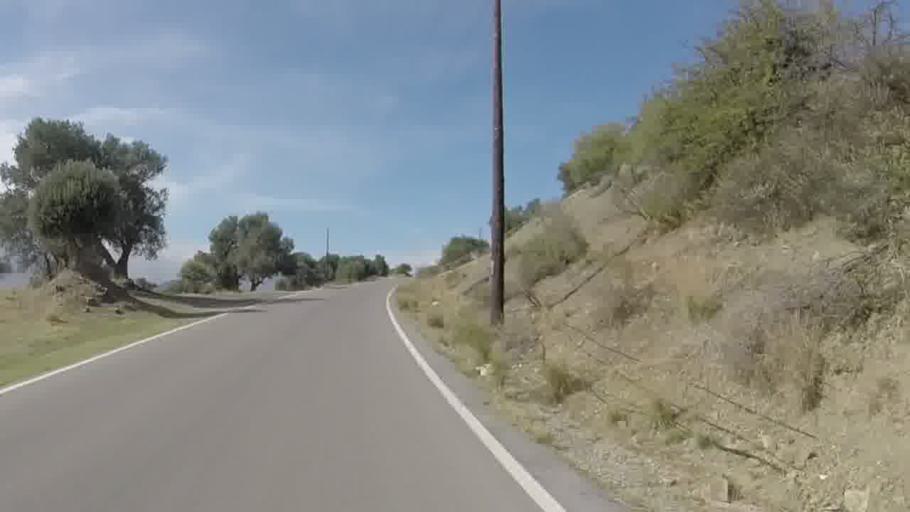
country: GR
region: Crete
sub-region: Nomos Rethymnis
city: Agia Galini
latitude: 35.1471
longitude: 24.7374
